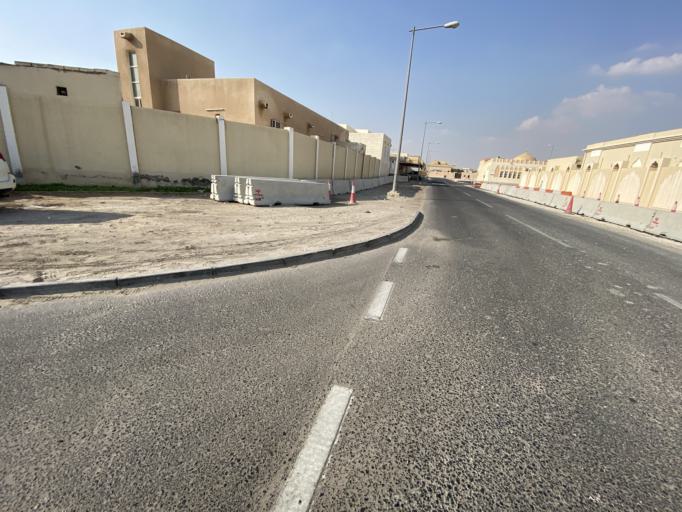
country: QA
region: Baladiyat ar Rayyan
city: Ar Rayyan
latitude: 25.2343
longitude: 51.3780
